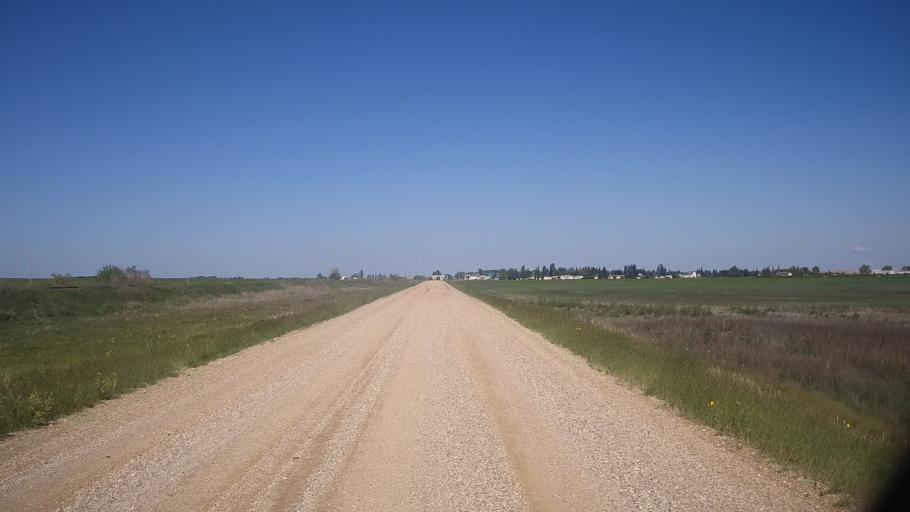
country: CA
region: Saskatchewan
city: Watrous
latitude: 51.8871
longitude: -106.0398
